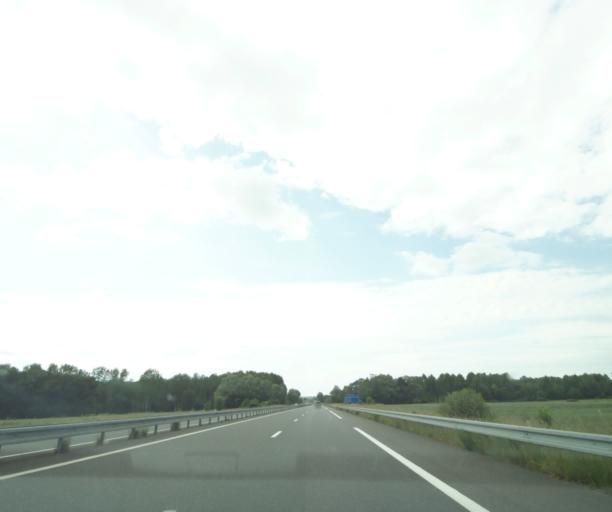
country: FR
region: Pays de la Loire
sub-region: Departement de Maine-et-Loire
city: Beaufort-en-Vallee
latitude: 47.4774
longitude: -0.2023
